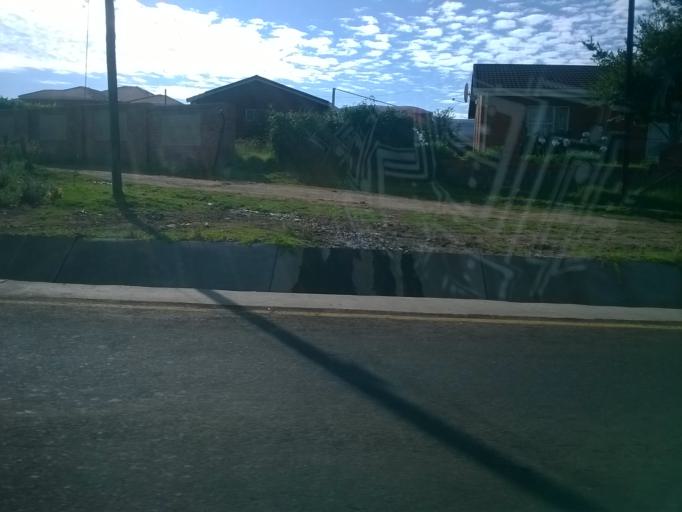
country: LS
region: Berea
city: Teyateyaneng
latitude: -29.1395
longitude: 27.7649
